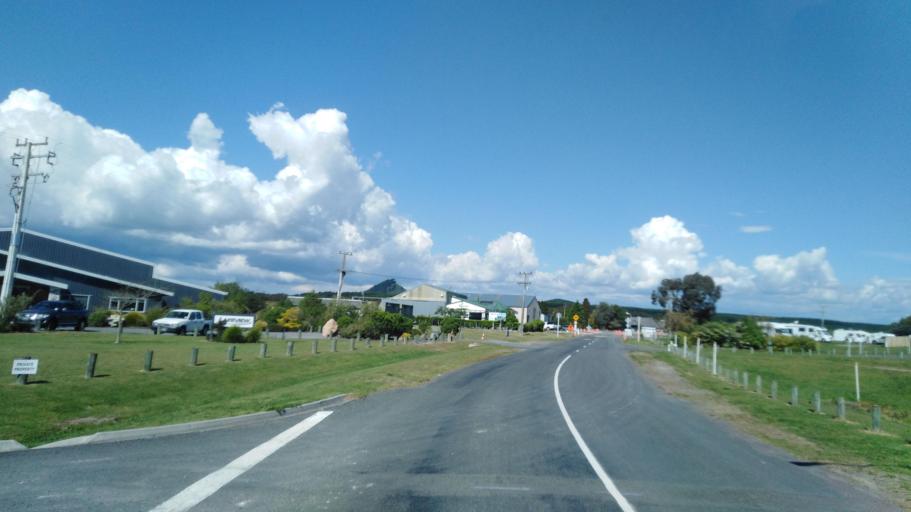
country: NZ
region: Waikato
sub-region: Taupo District
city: Taupo
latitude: -38.7387
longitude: 176.0795
